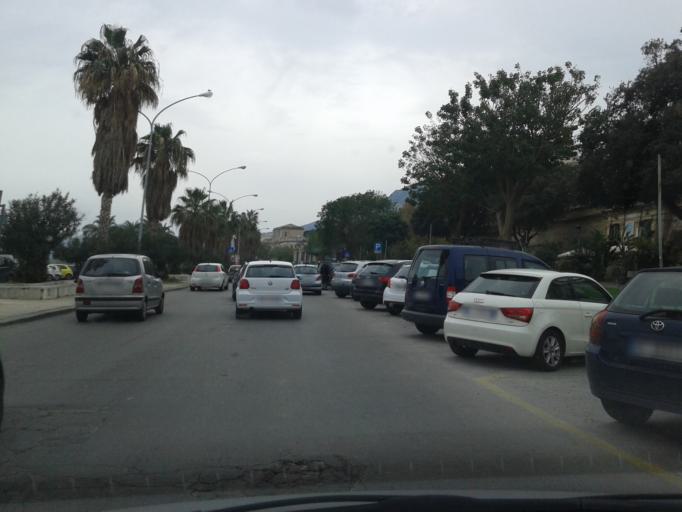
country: IT
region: Sicily
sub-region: Palermo
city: Palermo
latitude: 38.1195
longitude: 13.3717
